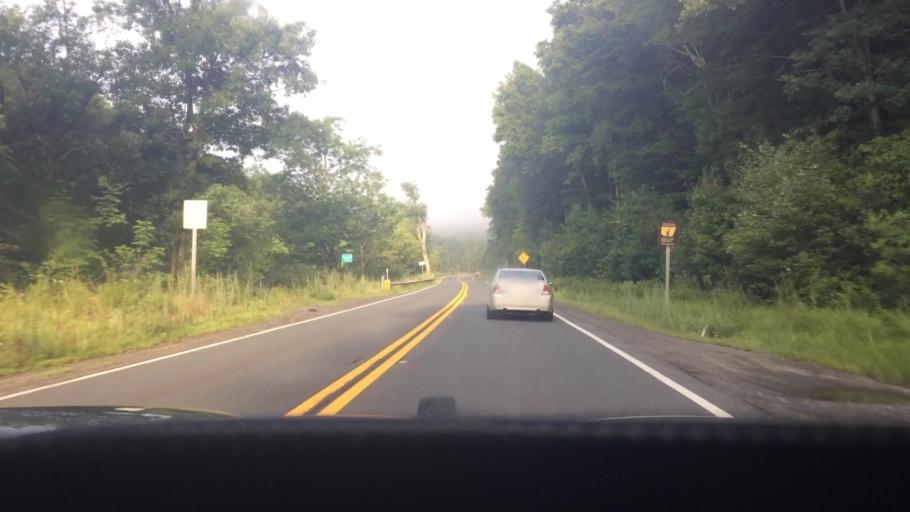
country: US
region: Massachusetts
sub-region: Franklin County
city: Erving
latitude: 42.6081
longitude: -72.4187
